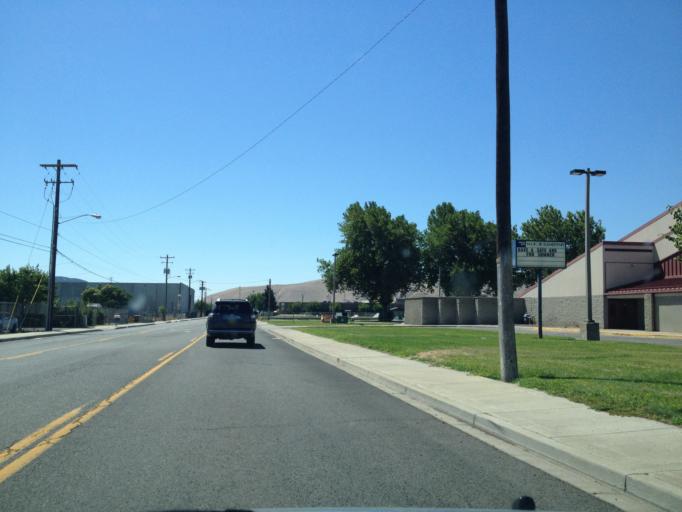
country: US
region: Washington
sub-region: Yakima County
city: Union Gap
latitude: 46.5734
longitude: -120.4778
